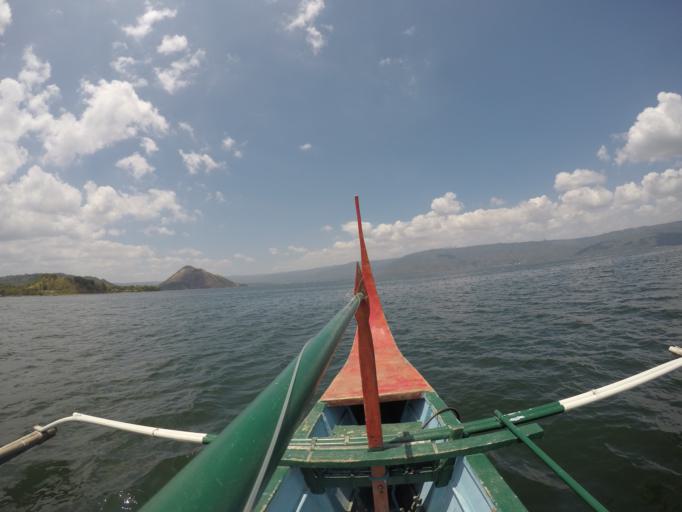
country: PH
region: Calabarzon
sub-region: Province of Batangas
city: Talisay
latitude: 14.0377
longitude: 121.0025
